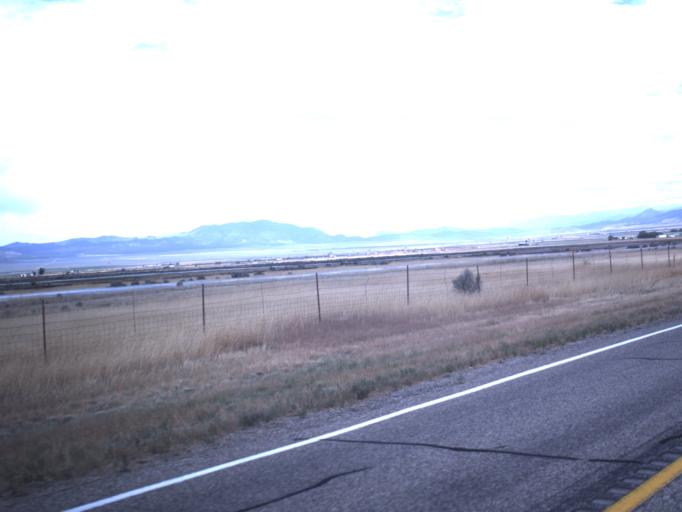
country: US
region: Utah
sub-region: Iron County
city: Parowan
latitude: 37.8585
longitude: -112.8148
